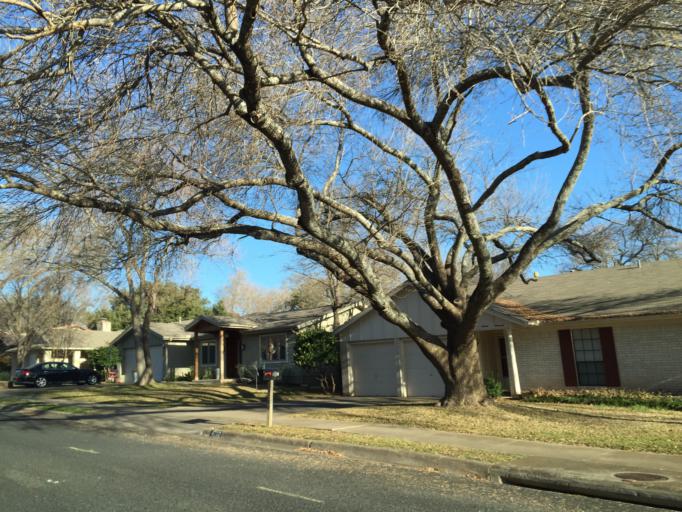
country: US
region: Texas
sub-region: Williamson County
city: Jollyville
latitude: 30.4103
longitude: -97.7376
